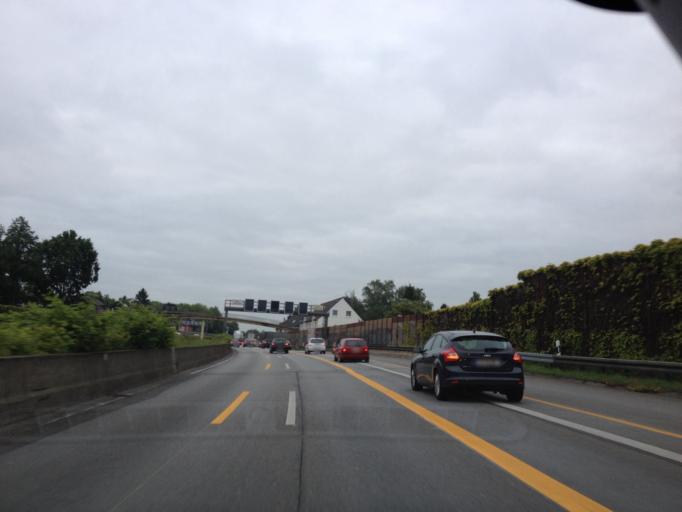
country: DE
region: North Rhine-Westphalia
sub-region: Regierungsbezirk Dusseldorf
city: Essen
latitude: 51.4552
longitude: 7.0441
